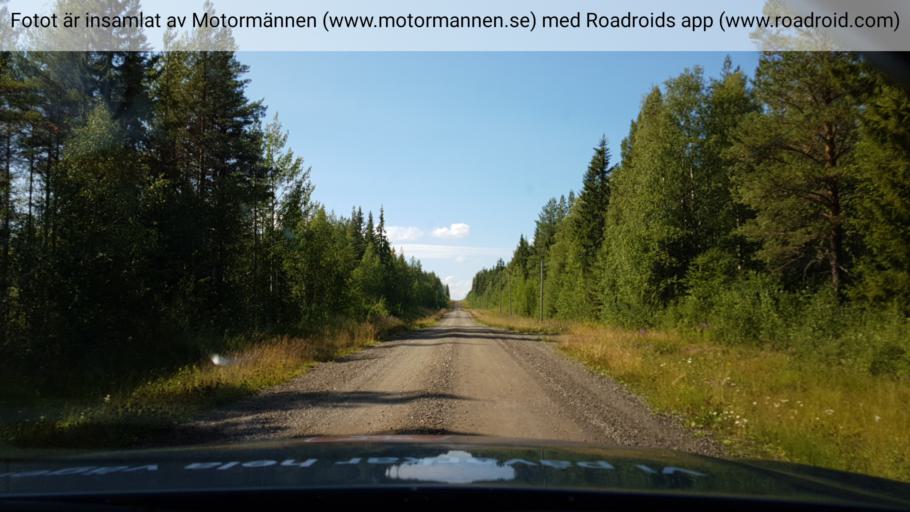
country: SE
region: Vaesterbotten
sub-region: Dorotea Kommun
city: Dorotea
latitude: 64.0916
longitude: 16.5158
